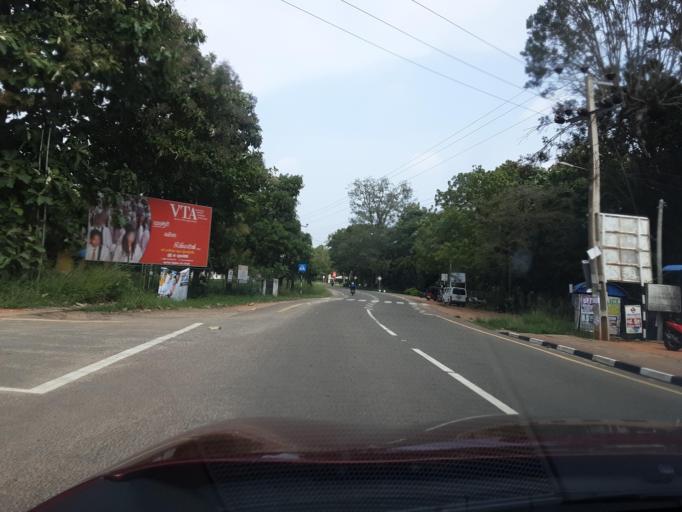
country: LK
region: North Central
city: Anuradhapura
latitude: 8.3595
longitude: 80.5114
